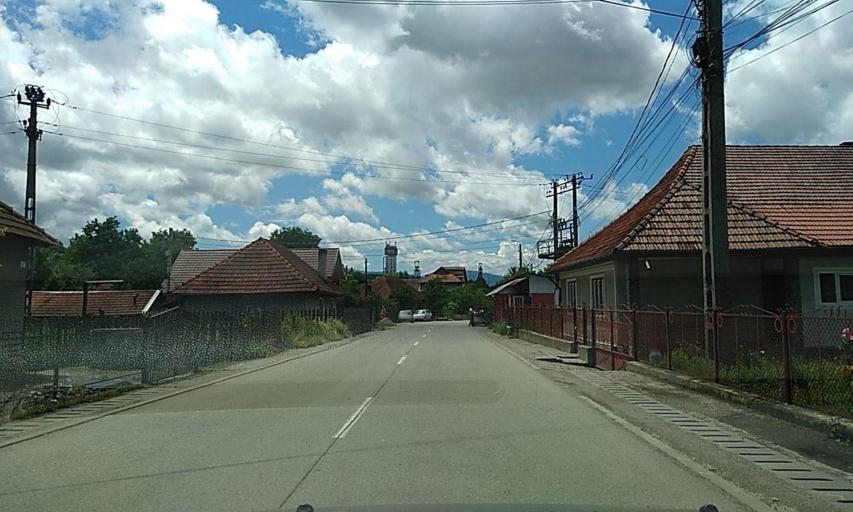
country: RO
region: Hunedoara
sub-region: Oras Petrila
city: Petrila
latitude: 45.4564
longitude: 23.4396
